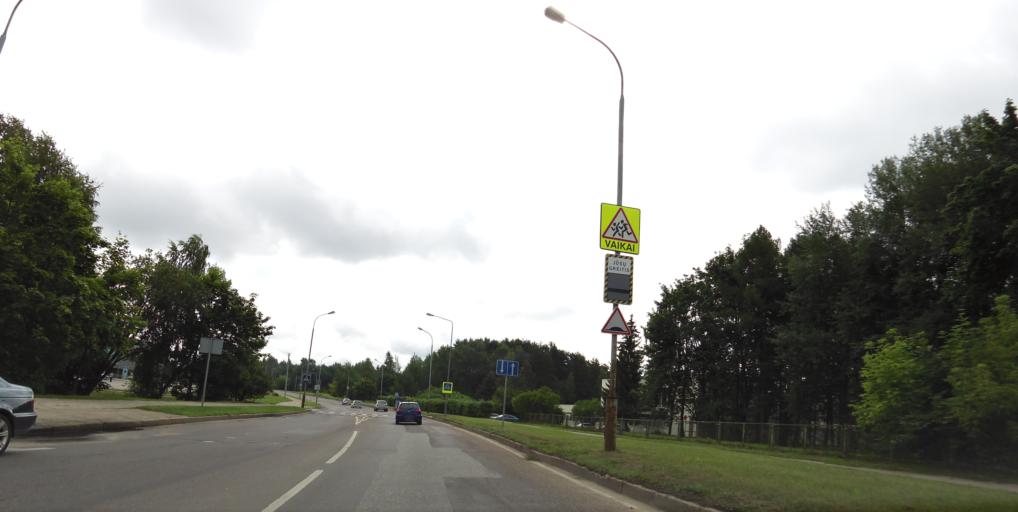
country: LT
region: Vilnius County
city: Seskine
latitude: 54.7051
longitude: 25.2338
